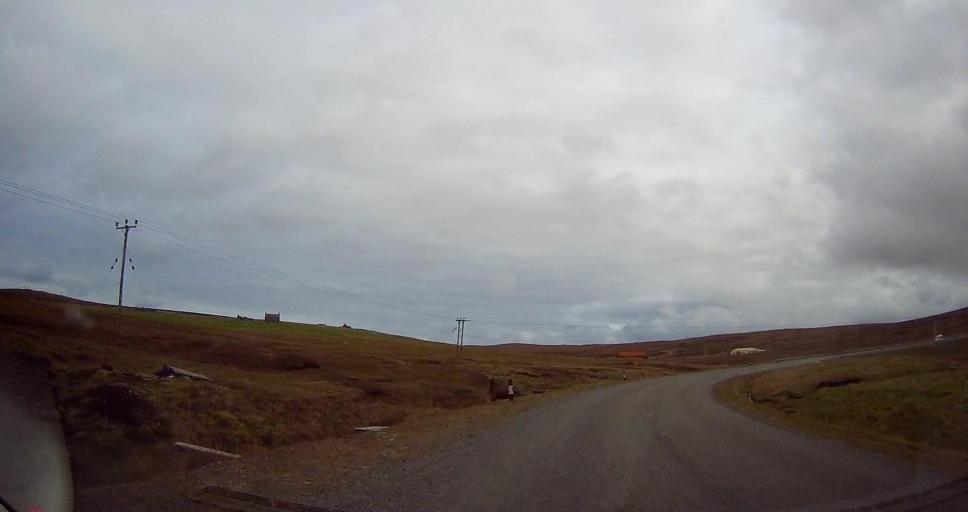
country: GB
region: Scotland
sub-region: Shetland Islands
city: Shetland
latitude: 60.6673
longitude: -1.0682
